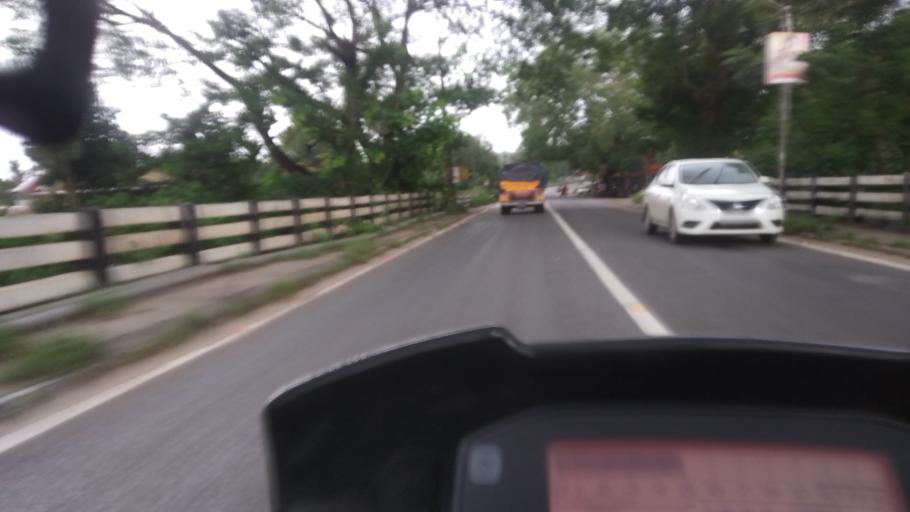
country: IN
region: Kerala
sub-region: Thiruvananthapuram
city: Attingal
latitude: 8.7099
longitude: 76.8130
